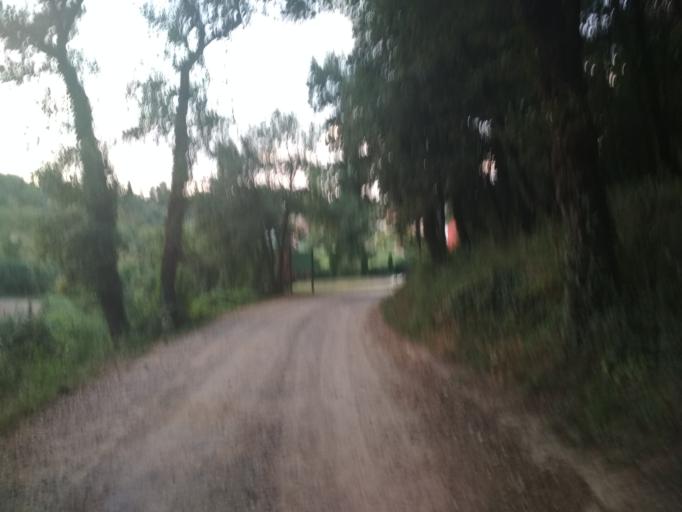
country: ES
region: Catalonia
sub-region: Provincia de Barcelona
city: Castelltercol
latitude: 41.7456
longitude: 2.1189
